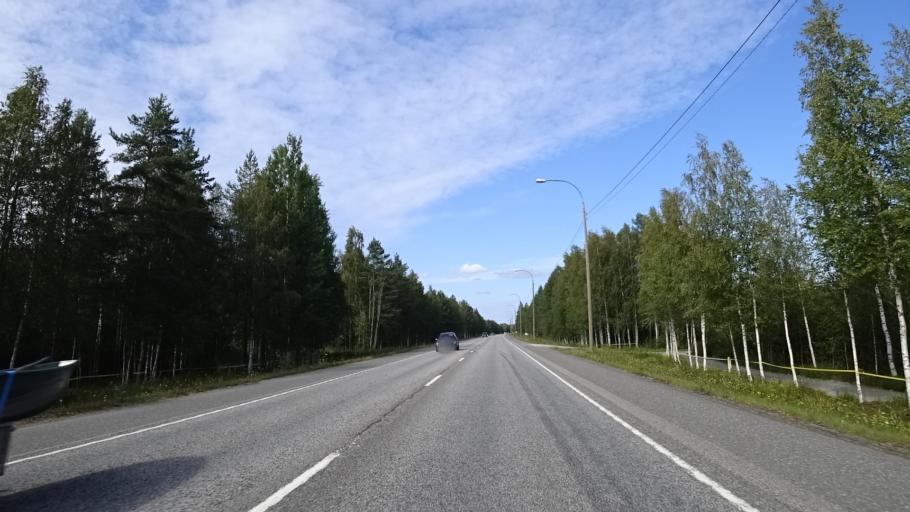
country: FI
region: North Karelia
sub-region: Joensuu
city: Joensuu
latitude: 62.6551
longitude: 29.7849
